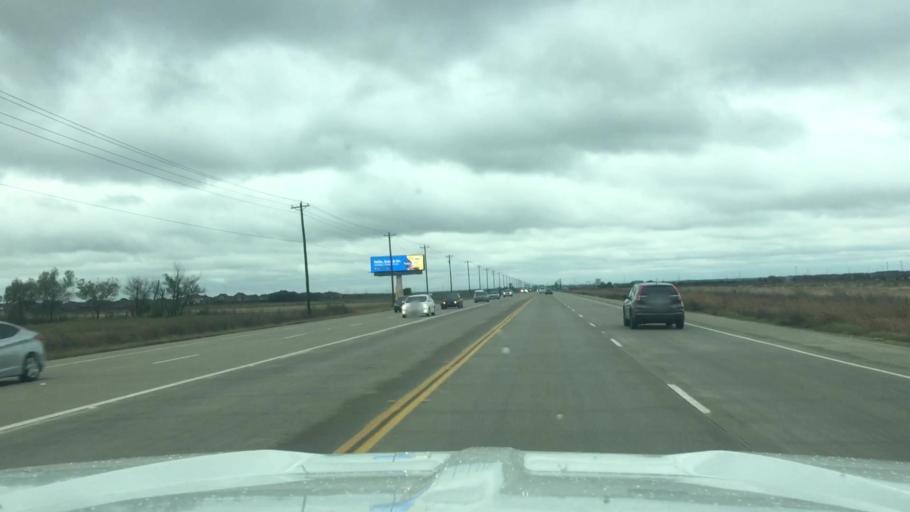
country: US
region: Texas
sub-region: Collin County
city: Prosper
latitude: 33.2193
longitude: -96.8614
